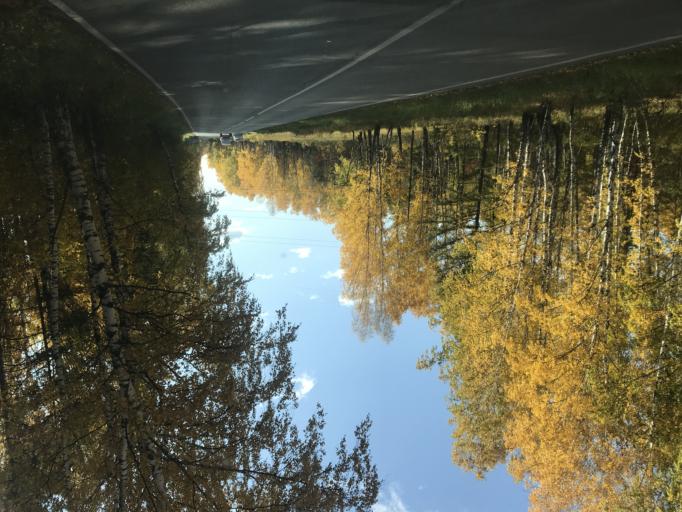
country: RU
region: Chelyabinsk
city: Dolgoderevenskoye
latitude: 55.2710
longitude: 61.3651
